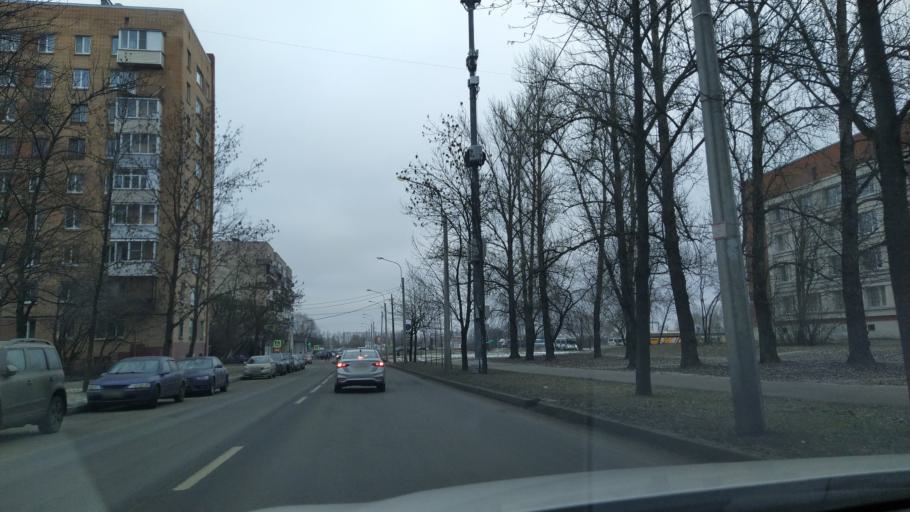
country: RU
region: St.-Petersburg
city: Pushkin
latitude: 59.7292
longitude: 30.4208
